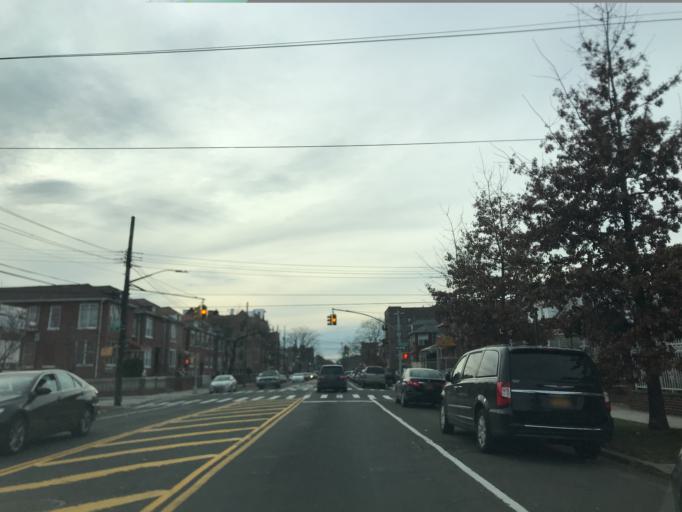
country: US
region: New York
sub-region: Kings County
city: Brooklyn
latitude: 40.6542
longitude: -73.9252
